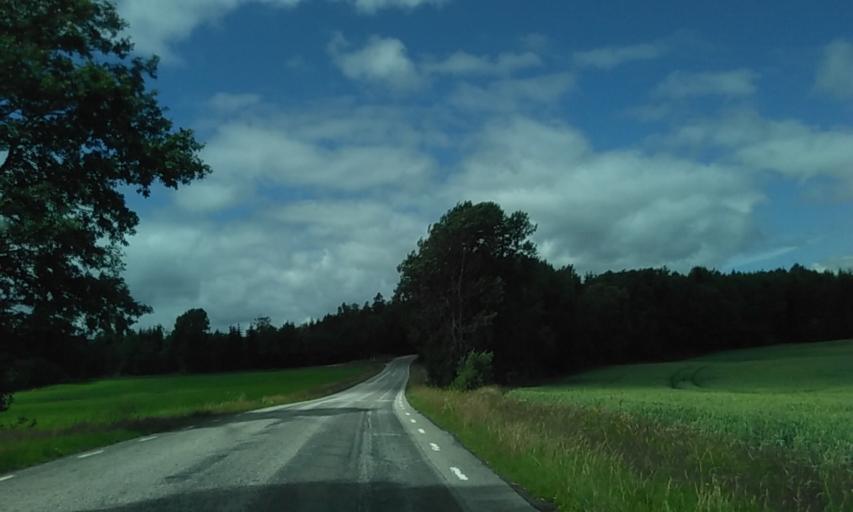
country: SE
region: Vaestra Goetaland
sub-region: Vargarda Kommun
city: Vargarda
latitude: 58.1008
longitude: 12.8270
